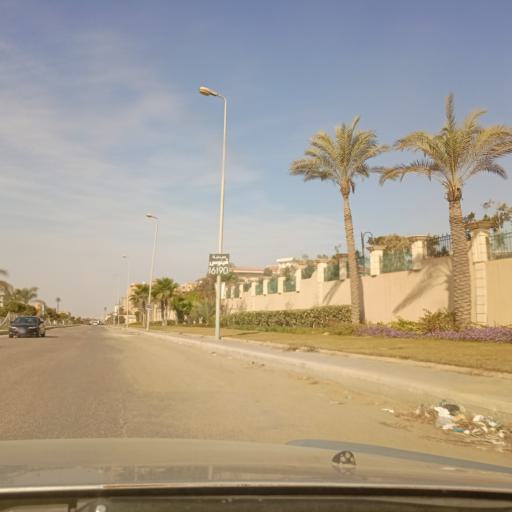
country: EG
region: Muhafazat al Qalyubiyah
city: Al Khankah
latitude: 30.0306
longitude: 31.4850
